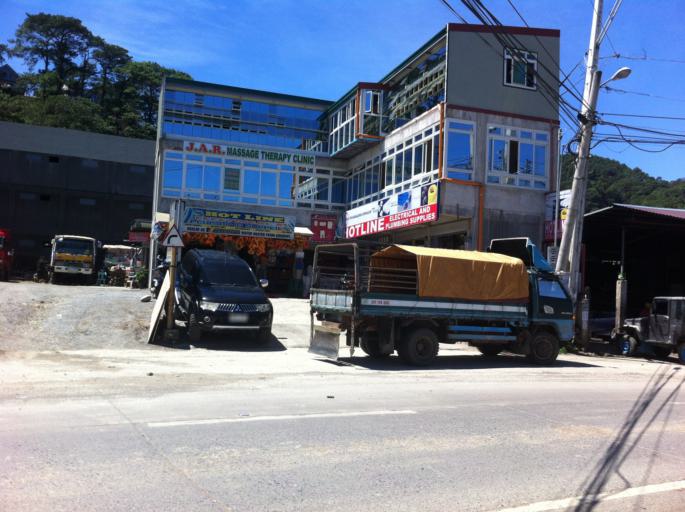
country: PH
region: Cordillera
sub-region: Province of Benguet
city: La Trinidad
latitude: 16.4461
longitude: 120.5778
